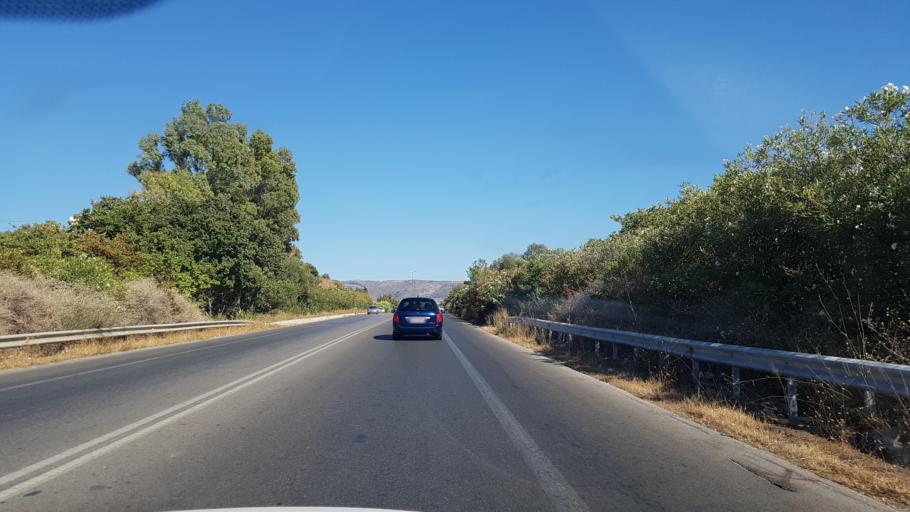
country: GR
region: Crete
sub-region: Nomos Chanias
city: Daratsos
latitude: 35.5022
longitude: 23.9852
